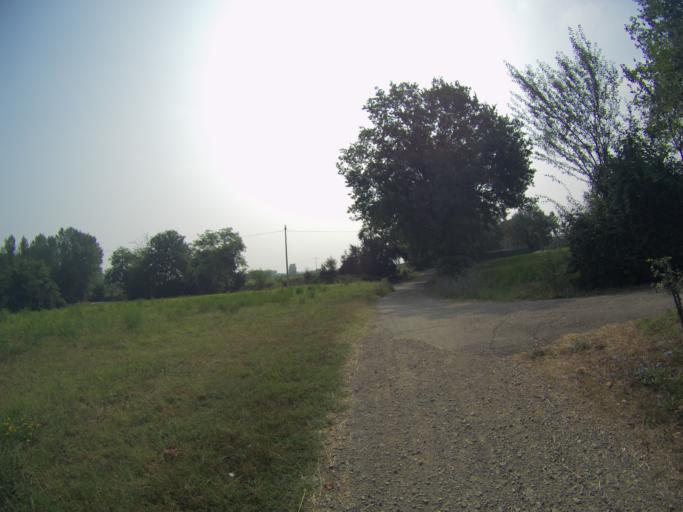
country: IT
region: Emilia-Romagna
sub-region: Provincia di Reggio Emilia
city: Borzano
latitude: 44.5974
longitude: 10.6481
